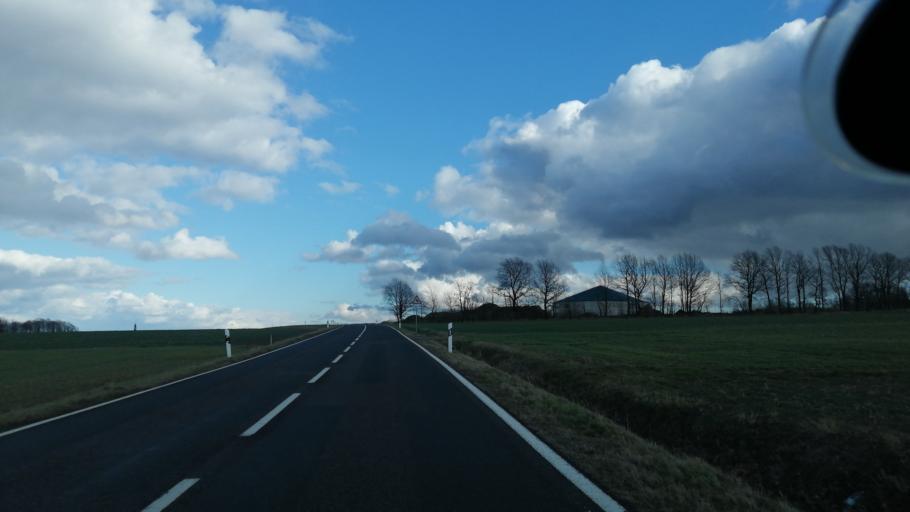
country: DE
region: Saxony
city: Hochkirch
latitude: 51.1443
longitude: 14.5515
